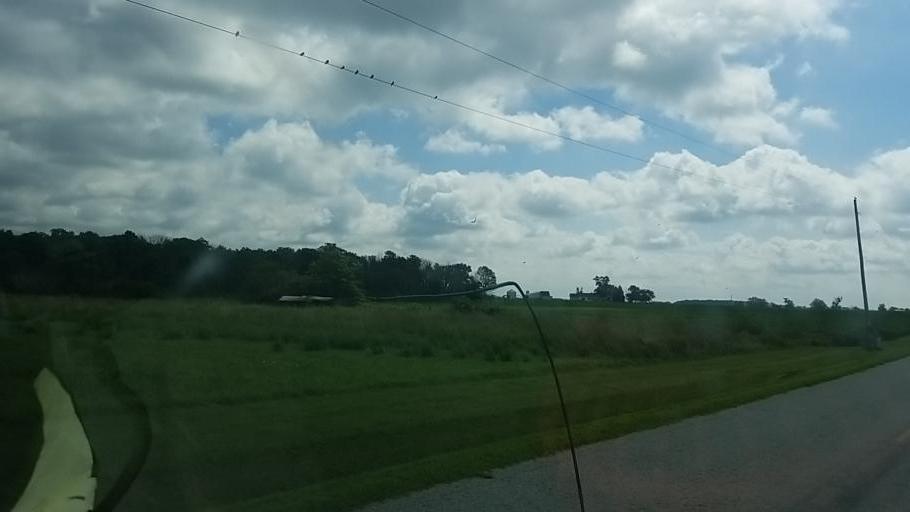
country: US
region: Ohio
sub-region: Madison County
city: Bethel
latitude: 39.7260
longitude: -83.4198
